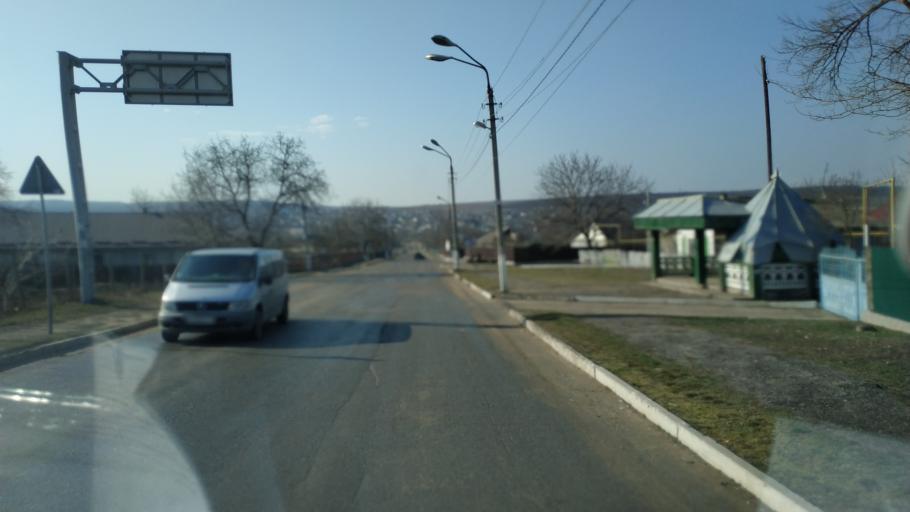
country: MD
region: Chisinau
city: Singera
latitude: 46.6870
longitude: 29.0516
